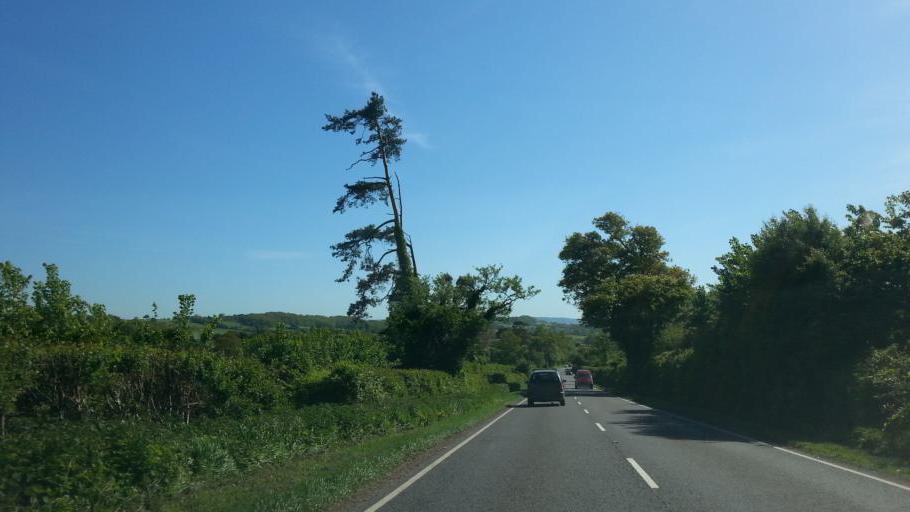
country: GB
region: England
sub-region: Somerset
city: Milborne Port
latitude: 50.9673
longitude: -2.4267
